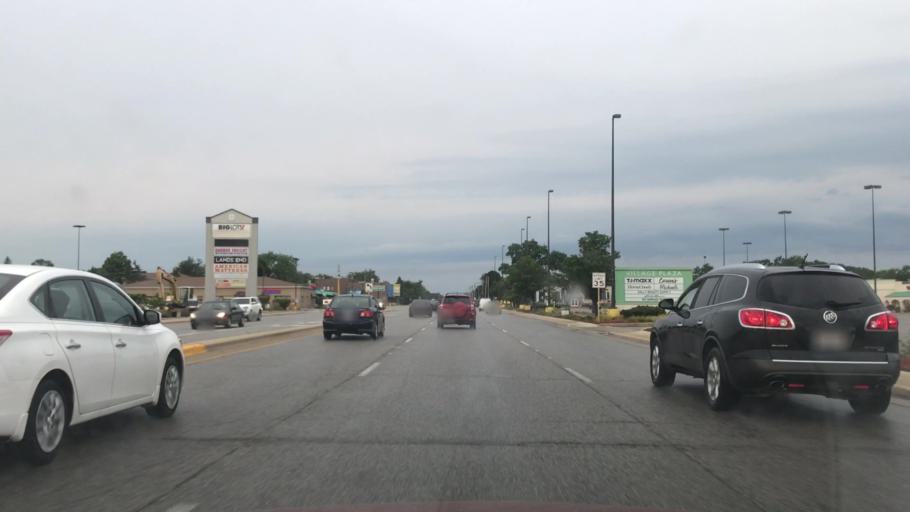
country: US
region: Illinois
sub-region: Cook County
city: Niles
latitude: 42.0409
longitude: -87.8067
